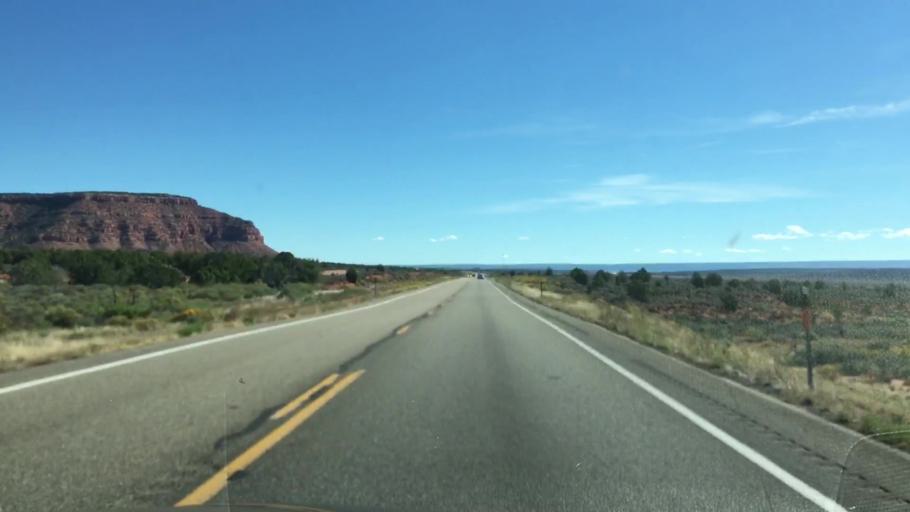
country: US
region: Utah
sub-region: Kane County
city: Kanab
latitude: 37.0278
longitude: -112.4784
